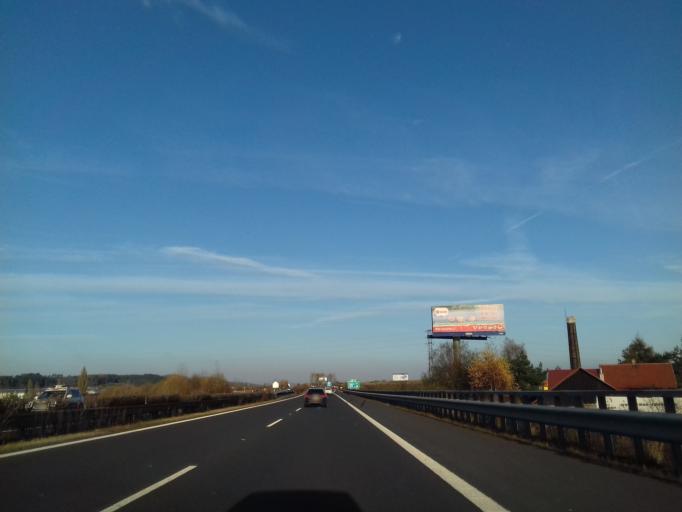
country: CZ
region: Central Bohemia
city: Zebrak
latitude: 49.8650
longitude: 13.8923
